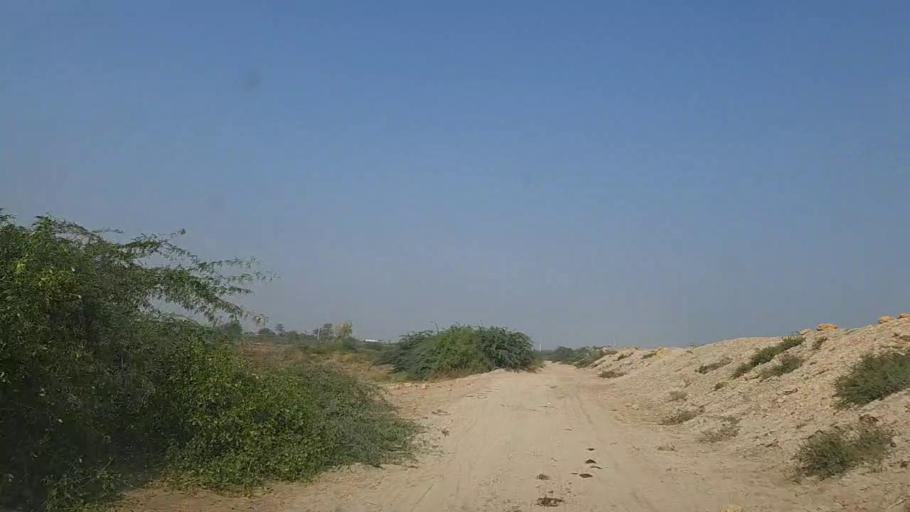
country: PK
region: Sindh
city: Thatta
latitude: 24.6600
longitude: 67.9265
